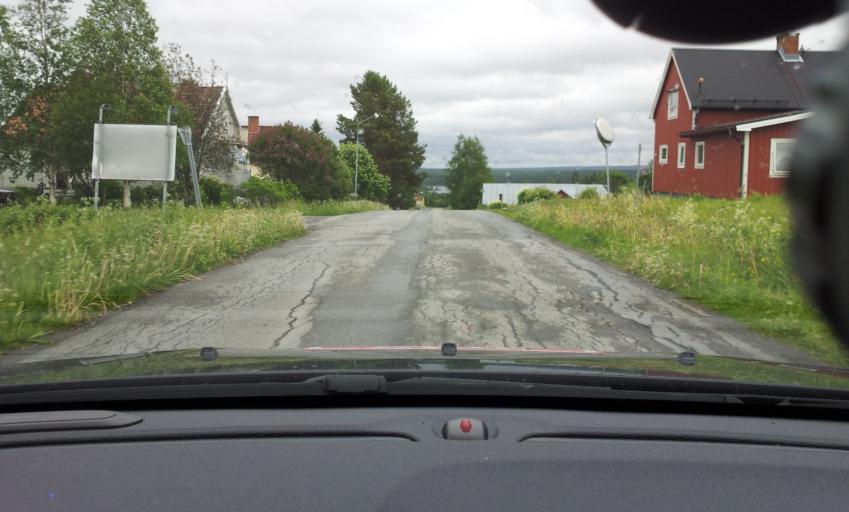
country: SE
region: Jaemtland
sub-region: Krokoms Kommun
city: Krokom
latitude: 63.6739
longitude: 14.6100
